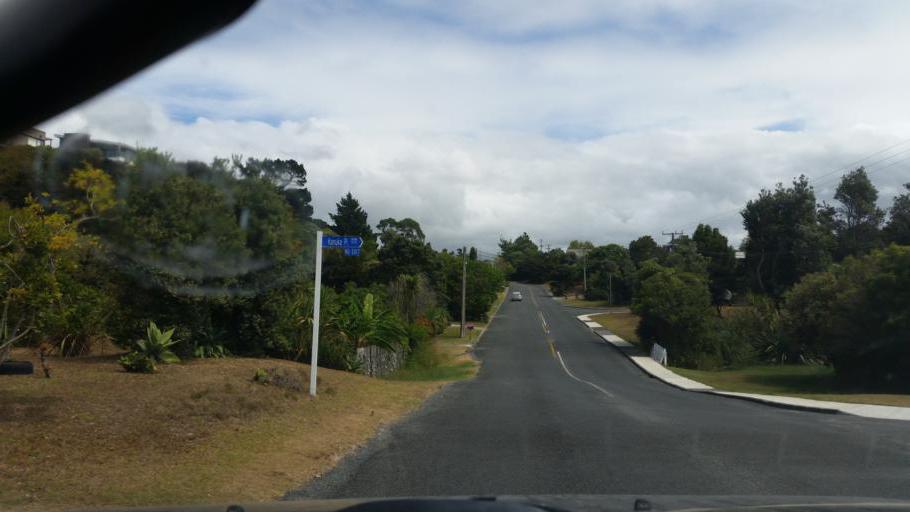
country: NZ
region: Auckland
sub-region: Auckland
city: Wellsford
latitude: -36.0866
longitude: 174.5859
